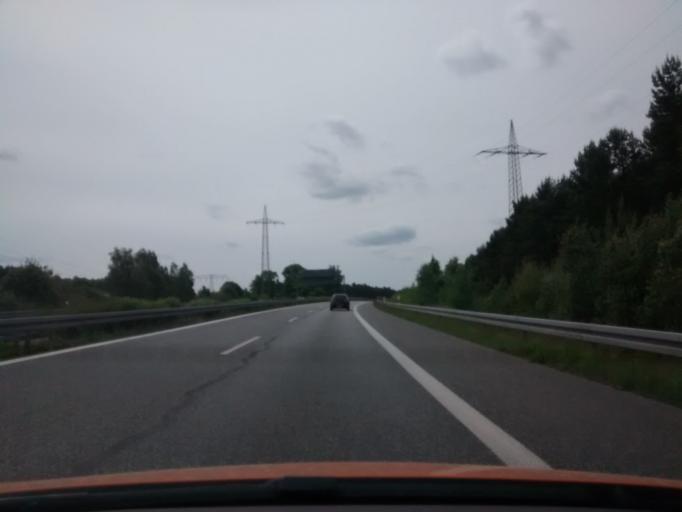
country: DE
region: Brandenburg
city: Ludwigsfelde
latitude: 52.2818
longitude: 13.2777
